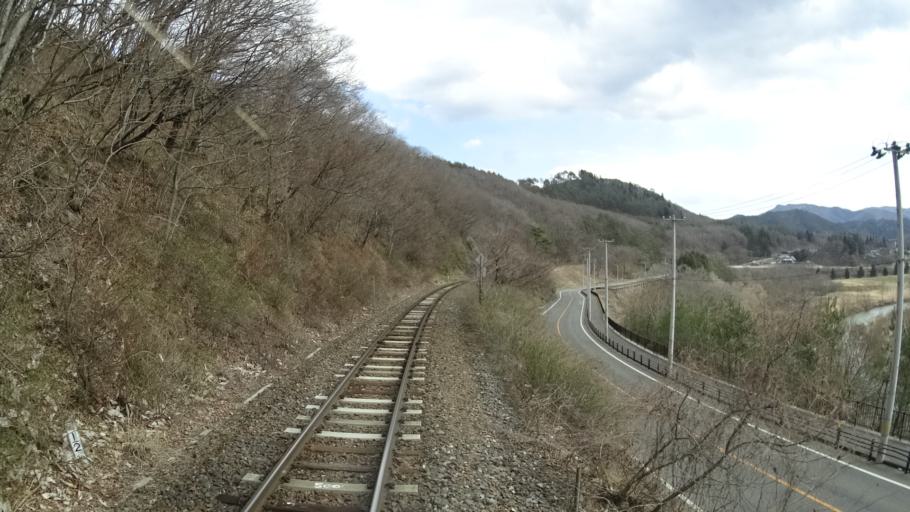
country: JP
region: Iwate
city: Tono
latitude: 39.3119
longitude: 141.3766
